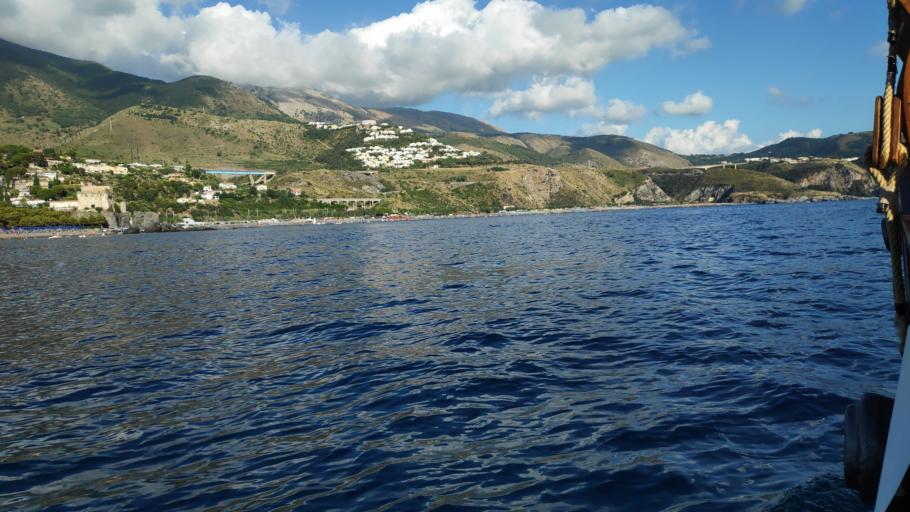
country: IT
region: Calabria
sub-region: Provincia di Cosenza
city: Praia a Mare
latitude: 39.8719
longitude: 15.7811
